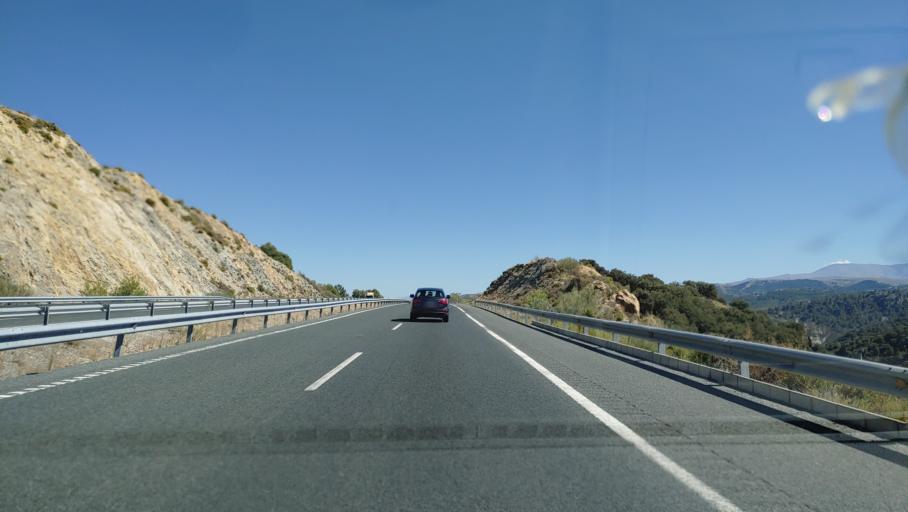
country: ES
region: Andalusia
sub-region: Provincia de Granada
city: Diezma
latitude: 37.3120
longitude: -3.3840
